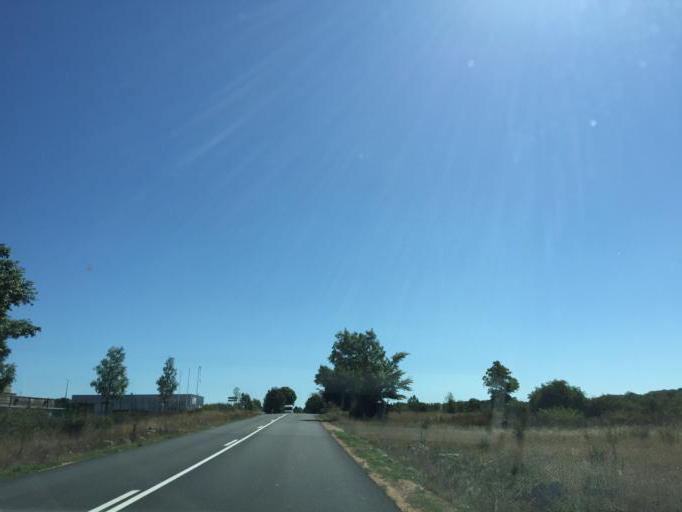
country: FR
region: Midi-Pyrenees
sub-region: Departement de l'Aveyron
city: La Cavalerie
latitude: 44.0129
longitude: 3.1281
